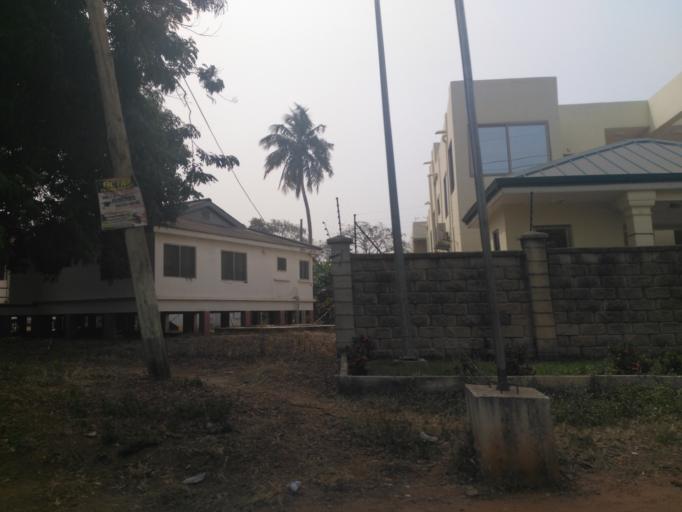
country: GH
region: Ashanti
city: Kumasi
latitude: 6.6879
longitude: -1.6318
